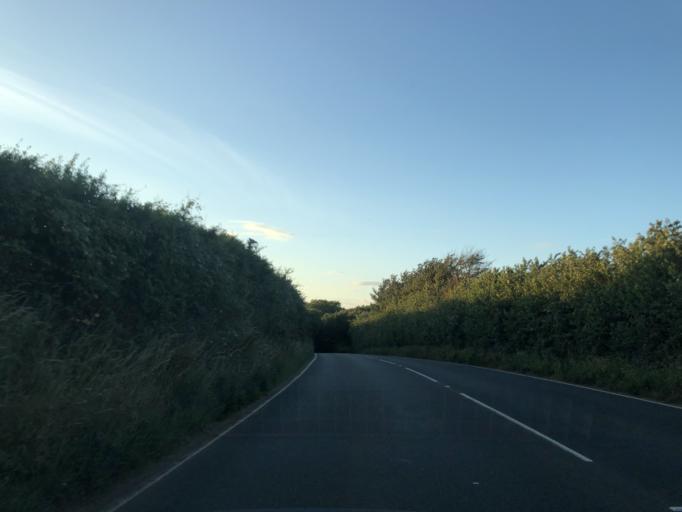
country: GB
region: England
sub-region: Isle of Wight
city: Newport
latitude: 50.6631
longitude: -1.2847
